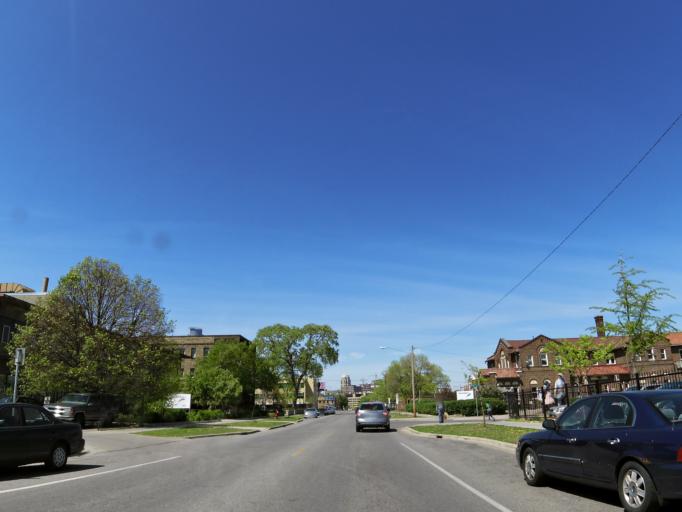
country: US
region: Minnesota
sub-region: Hennepin County
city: Minneapolis
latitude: 44.9635
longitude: -93.2625
